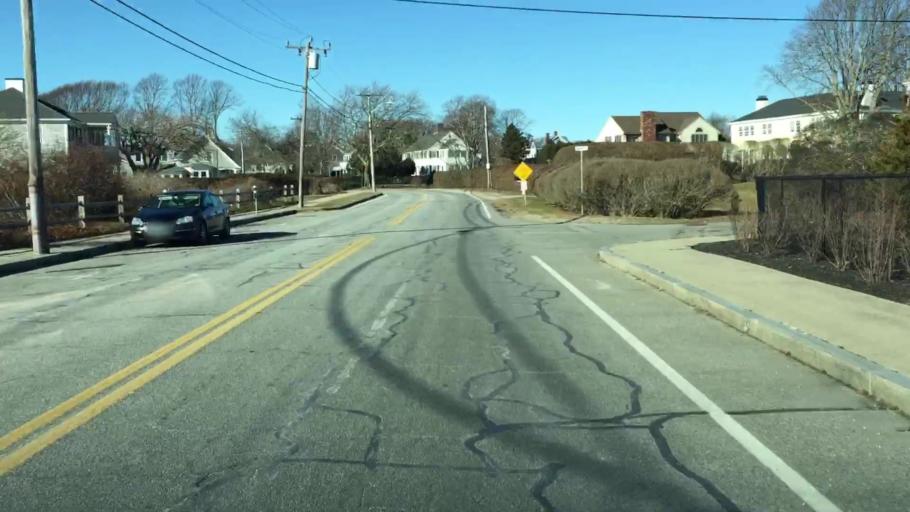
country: US
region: Massachusetts
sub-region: Barnstable County
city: Falmouth
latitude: 41.5443
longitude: -70.6075
